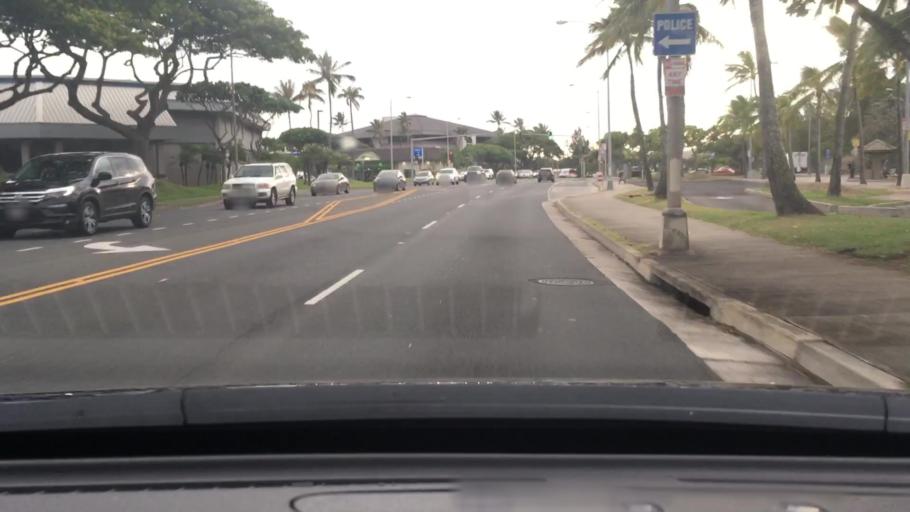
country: US
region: Hawaii
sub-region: Honolulu County
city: Waimanalo Beach
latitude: 21.2842
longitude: -157.7120
